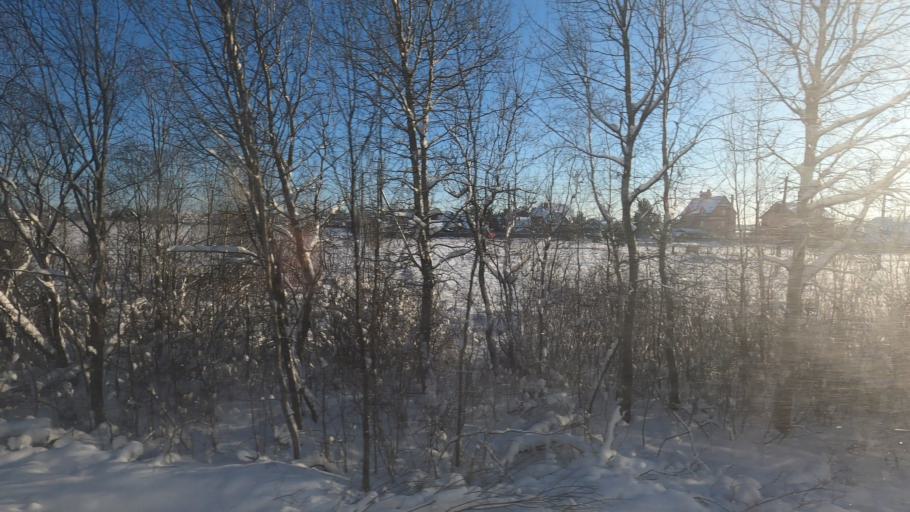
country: RU
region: Moskovskaya
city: Orud'yevo
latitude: 56.4380
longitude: 37.5084
